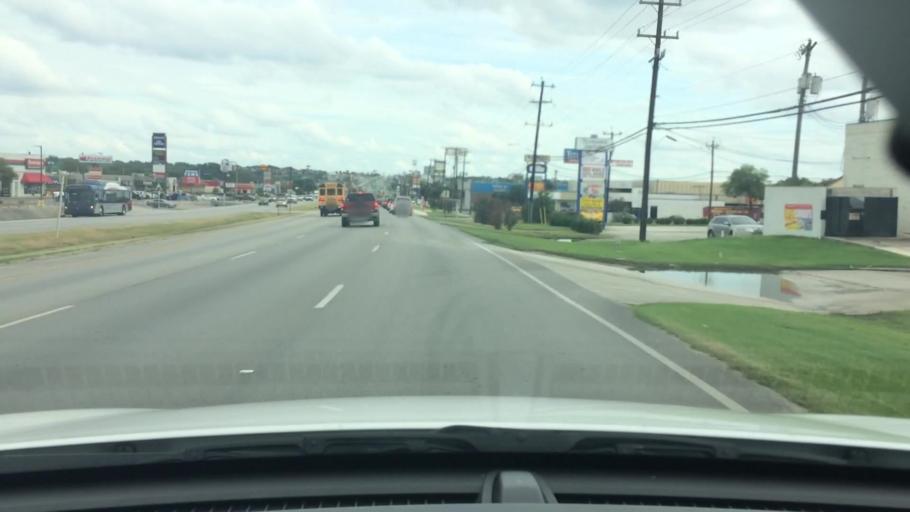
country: US
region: Texas
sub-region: Bexar County
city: Leon Valley
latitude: 29.4987
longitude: -98.6235
